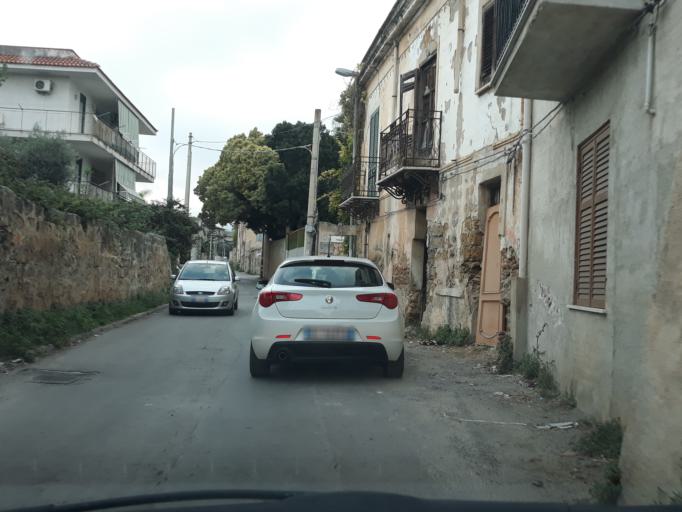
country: IT
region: Sicily
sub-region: Palermo
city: Monreale
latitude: 38.0926
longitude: 13.3165
